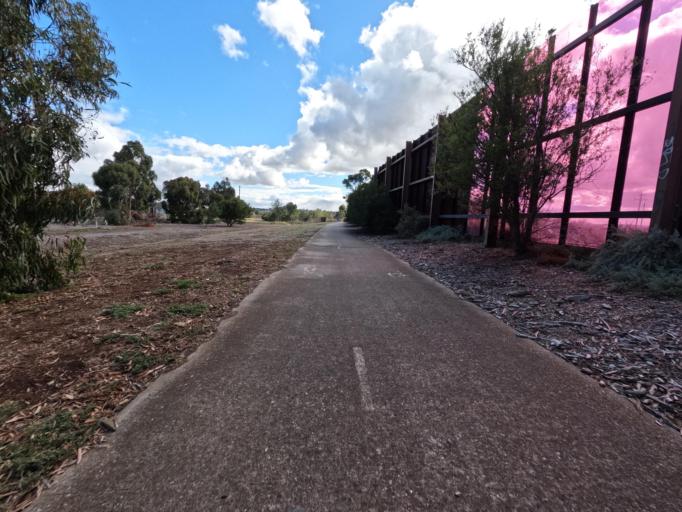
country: AU
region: Victoria
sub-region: Greater Geelong
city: Lara
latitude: -38.0602
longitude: 144.3700
